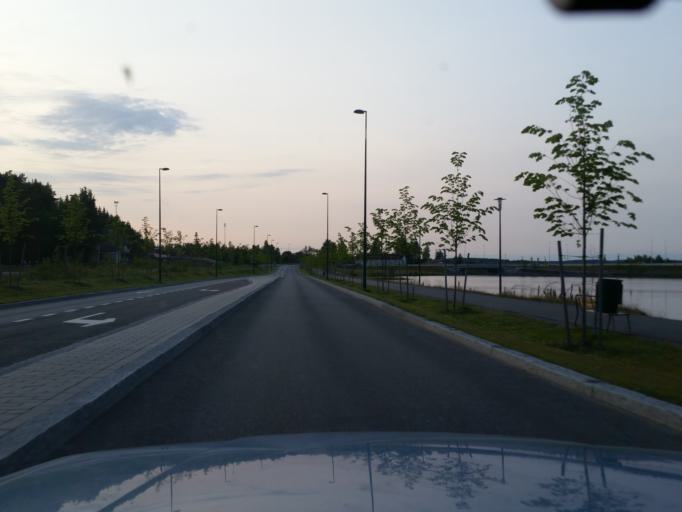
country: FI
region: Southern Savonia
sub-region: Savonlinna
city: Savonlinna
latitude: 61.8728
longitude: 28.8751
